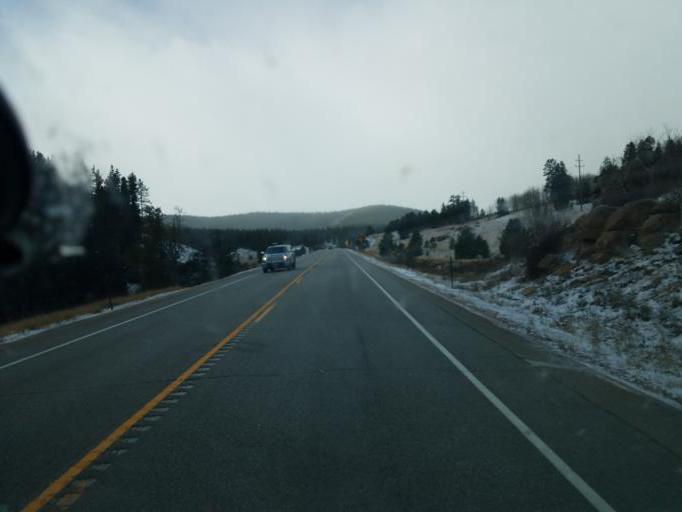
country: US
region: Colorado
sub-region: Clear Creek County
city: Georgetown
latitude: 39.4351
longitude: -105.7559
